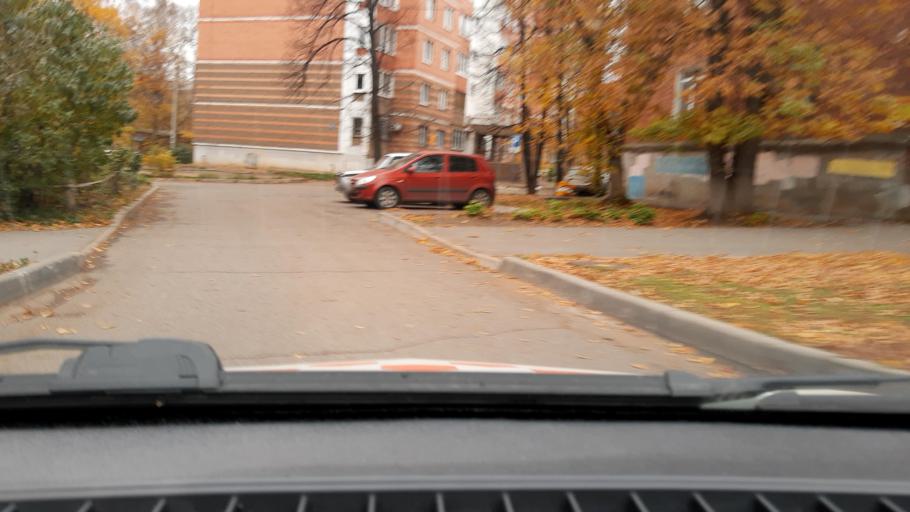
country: RU
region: Bashkortostan
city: Ufa
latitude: 54.8169
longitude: 56.1056
